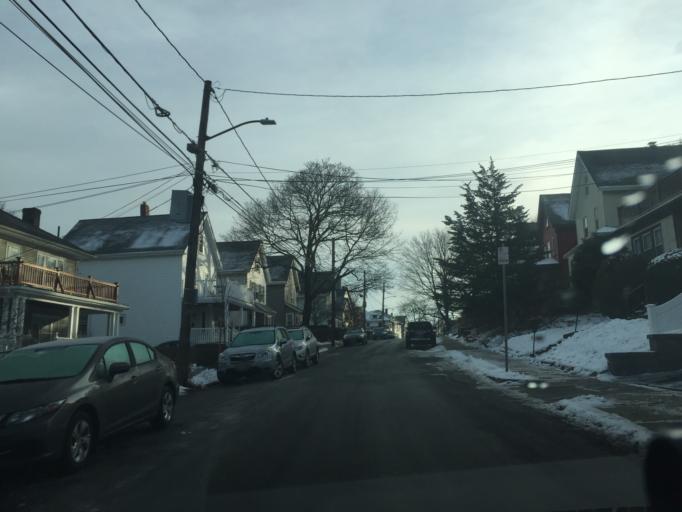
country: US
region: Massachusetts
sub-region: Middlesex County
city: Watertown
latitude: 42.3519
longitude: -71.1567
